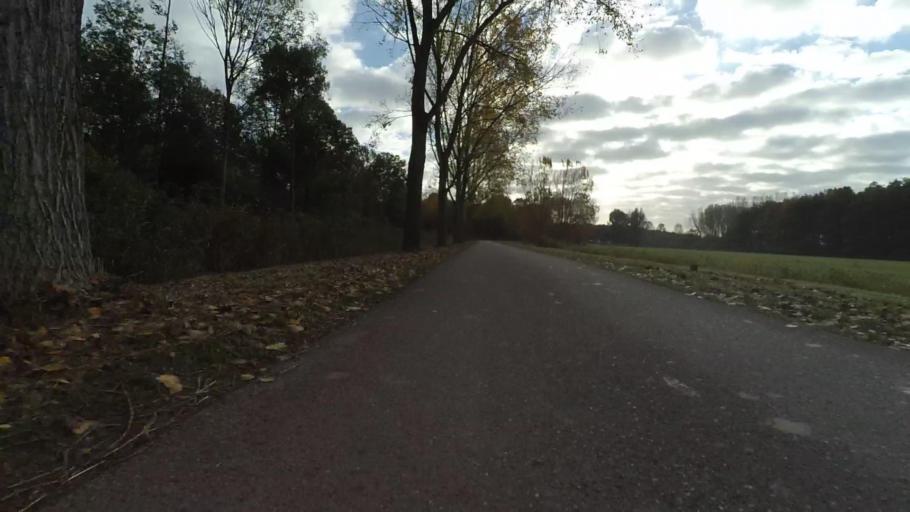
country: NL
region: North Holland
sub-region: Gemeente Huizen
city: Huizen
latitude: 52.3208
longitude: 5.2973
